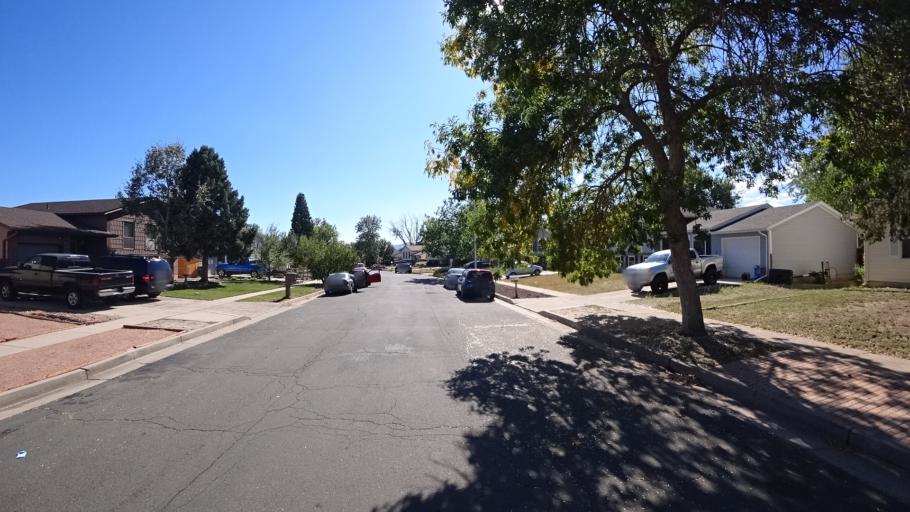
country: US
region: Colorado
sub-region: El Paso County
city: Stratmoor
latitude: 38.7981
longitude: -104.7506
